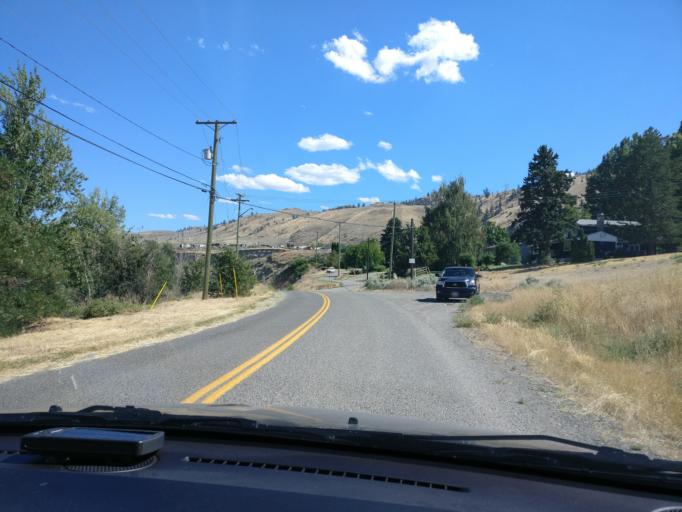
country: CA
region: British Columbia
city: Logan Lake
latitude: 50.7537
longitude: -120.8611
